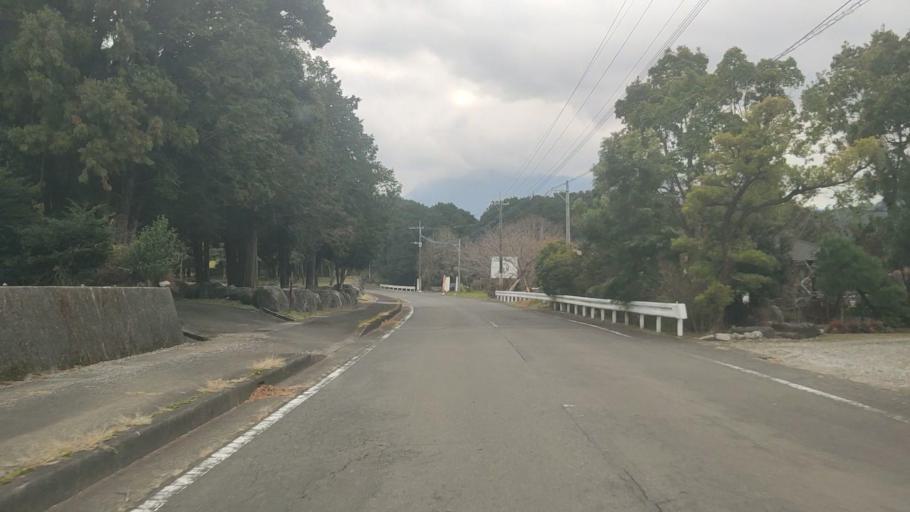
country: JP
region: Nagasaki
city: Shimabara
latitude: 32.8198
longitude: 130.2912
